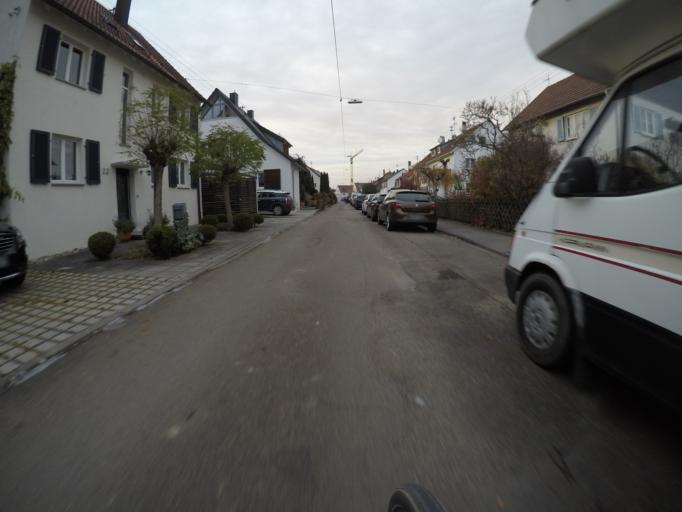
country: DE
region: Baden-Wuerttemberg
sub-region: Regierungsbezirk Stuttgart
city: Ostfildern
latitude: 48.7315
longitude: 9.2585
